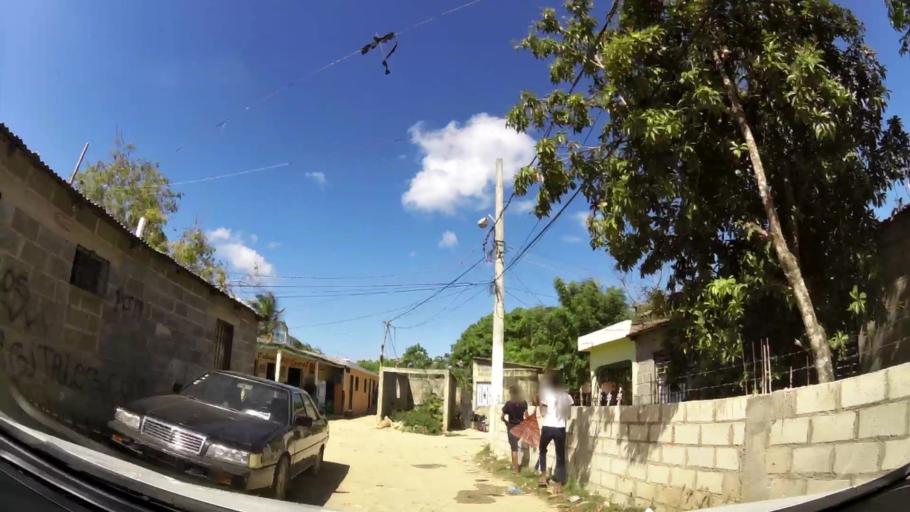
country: DO
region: Santo Domingo
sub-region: Santo Domingo
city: Boca Chica
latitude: 18.4582
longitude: -69.6265
